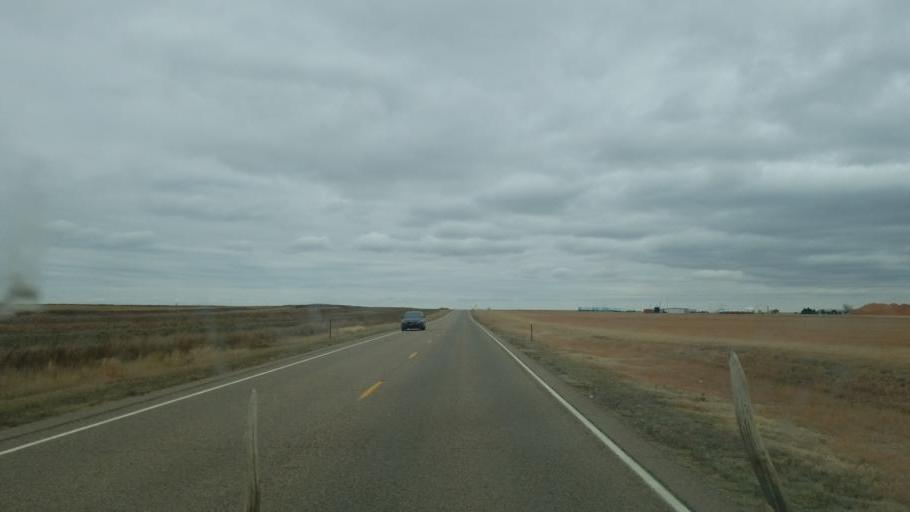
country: US
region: Colorado
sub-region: Cheyenne County
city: Cheyenne Wells
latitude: 38.8309
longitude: -102.3027
